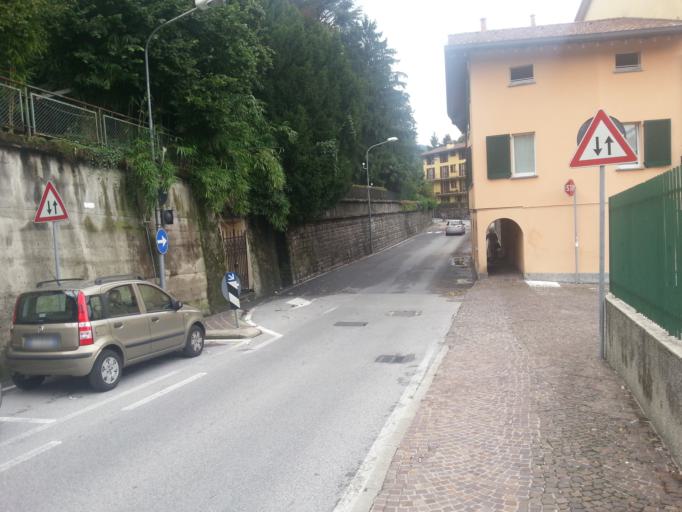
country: IT
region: Lombardy
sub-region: Provincia di Lecco
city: Galbiate
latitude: 45.8162
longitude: 9.3749
